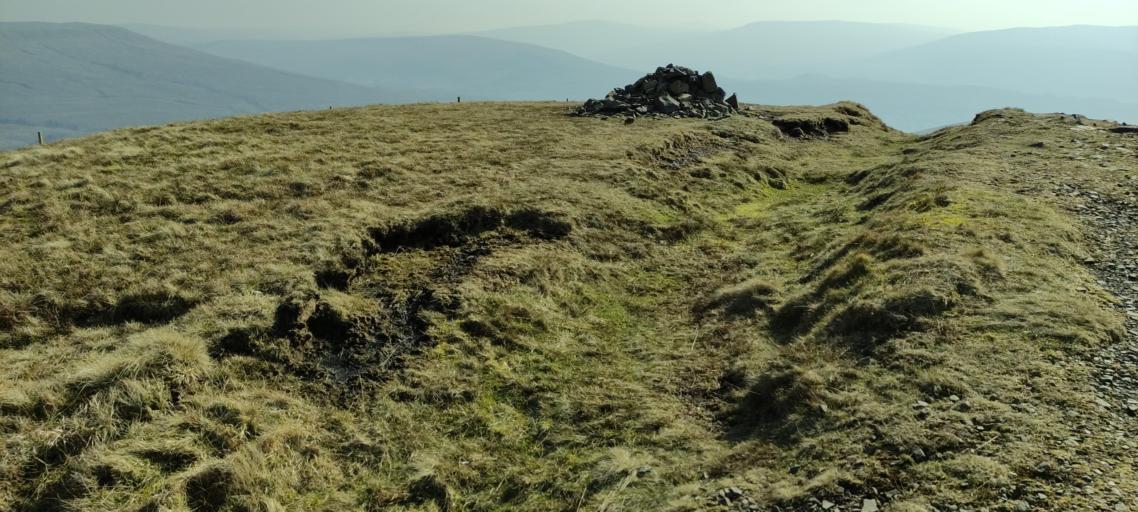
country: GB
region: England
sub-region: Cumbria
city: Sedbergh
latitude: 54.3586
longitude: -2.5081
